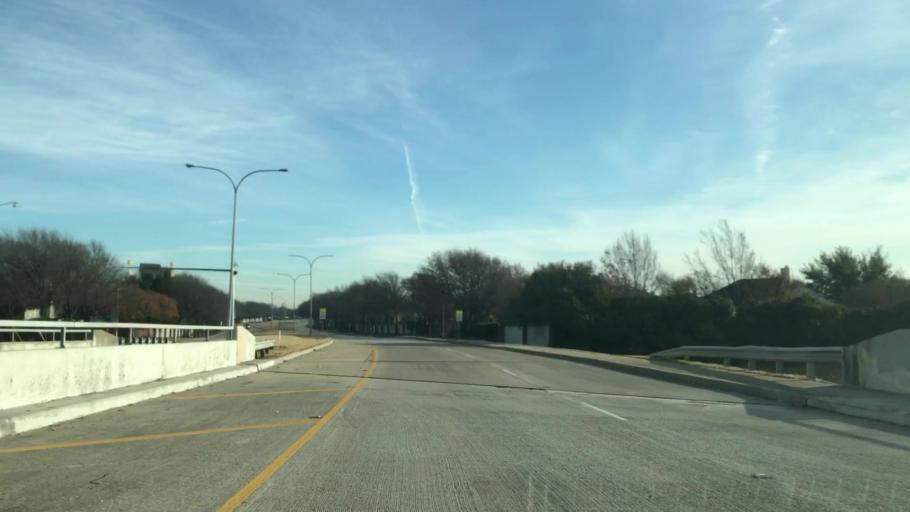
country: US
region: Texas
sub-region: Tarrant County
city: Watauga
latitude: 32.8718
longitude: -97.2762
